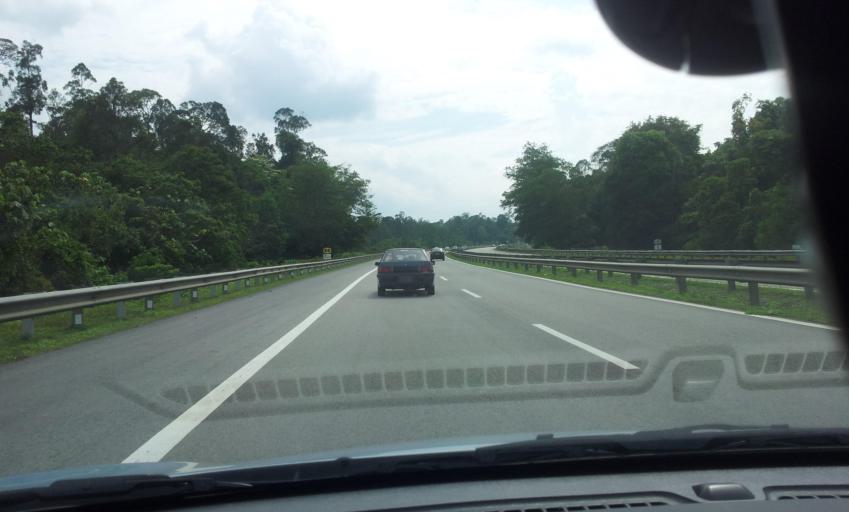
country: MY
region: Pahang
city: Kuantan
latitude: 3.7271
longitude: 102.9751
